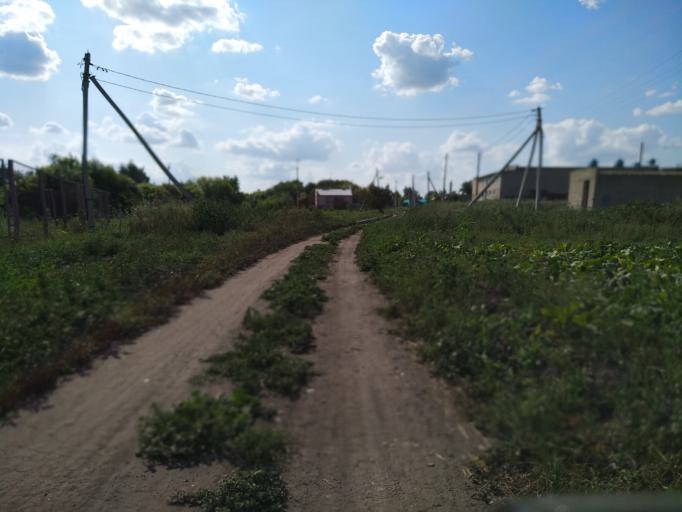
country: RU
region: Lipetsk
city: Dobrinka
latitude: 52.0365
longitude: 40.5570
